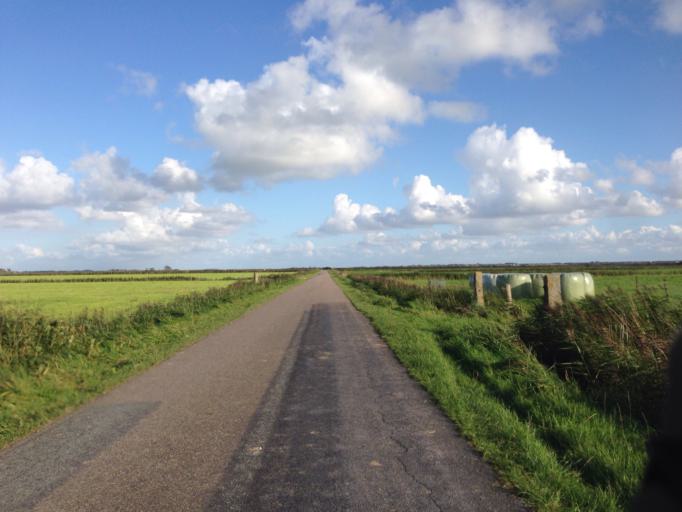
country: DE
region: Schleswig-Holstein
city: Oldsum
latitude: 54.7315
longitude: 8.4731
